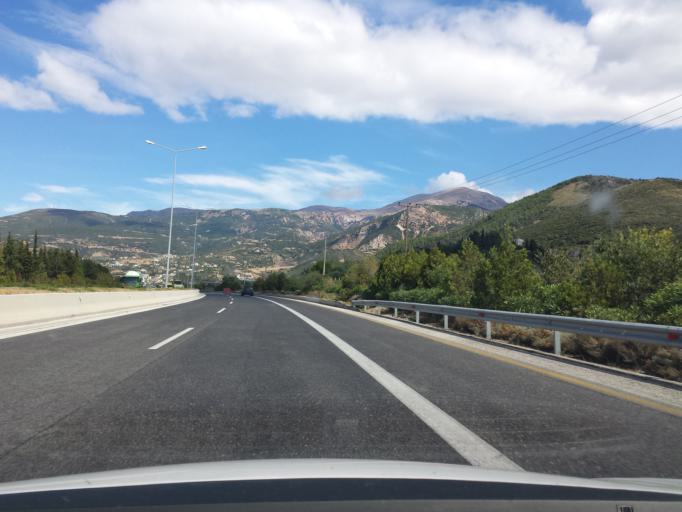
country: GR
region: West Greece
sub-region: Nomos Achaias
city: Ovria
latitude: 38.1965
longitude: 21.7619
